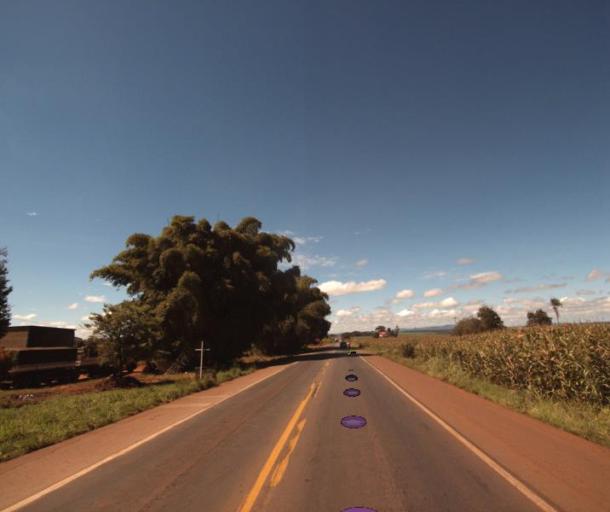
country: BR
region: Goias
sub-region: Rialma
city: Rialma
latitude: -15.3604
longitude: -49.5636
